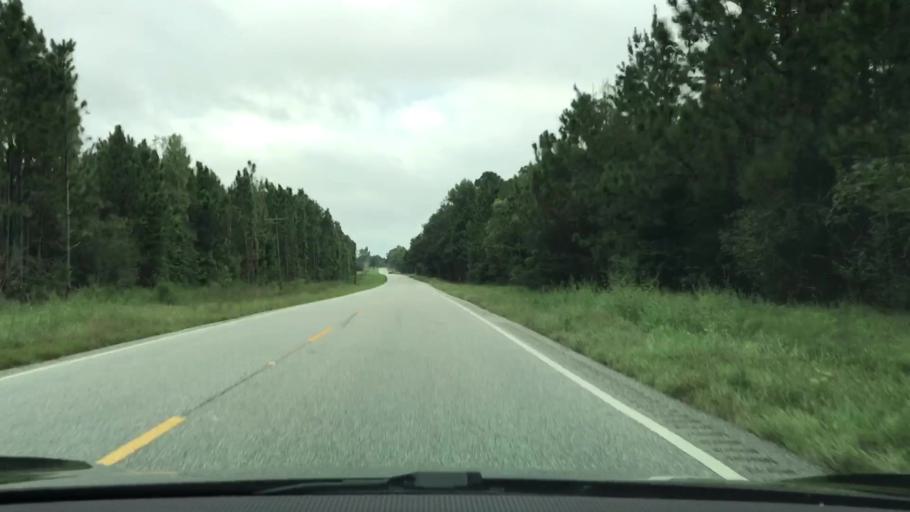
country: US
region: Alabama
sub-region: Geneva County
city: Samson
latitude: 31.0502
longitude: -86.1010
